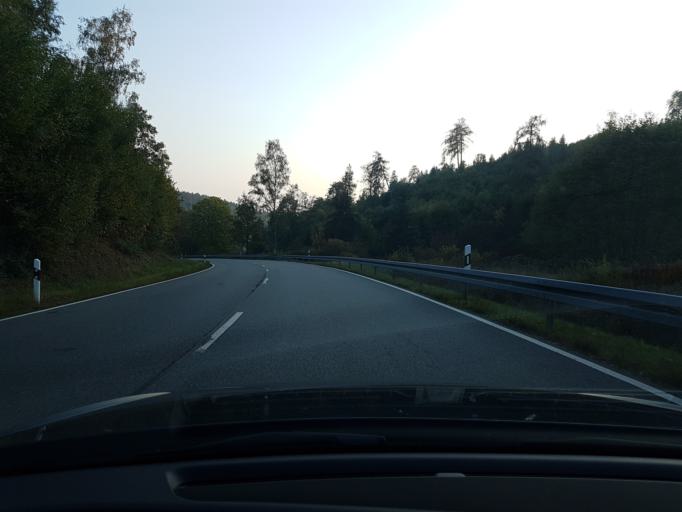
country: DE
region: Hesse
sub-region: Regierungsbezirk Darmstadt
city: Beerfelden
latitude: 49.5538
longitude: 8.9746
